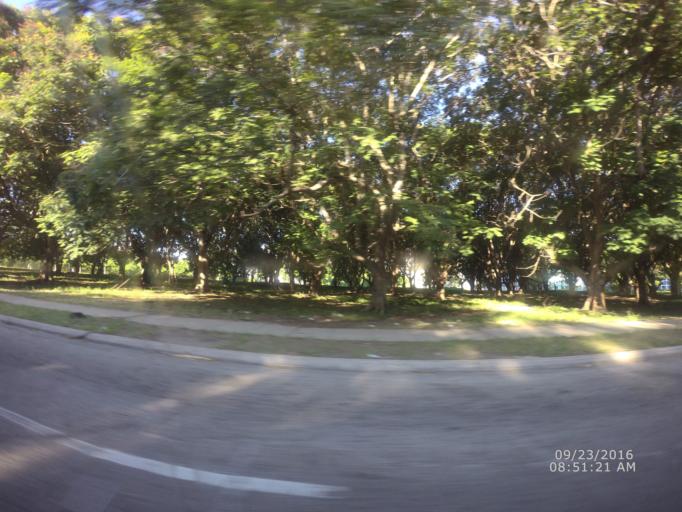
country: CU
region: La Habana
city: Cerro
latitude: 23.1191
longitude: -82.3885
